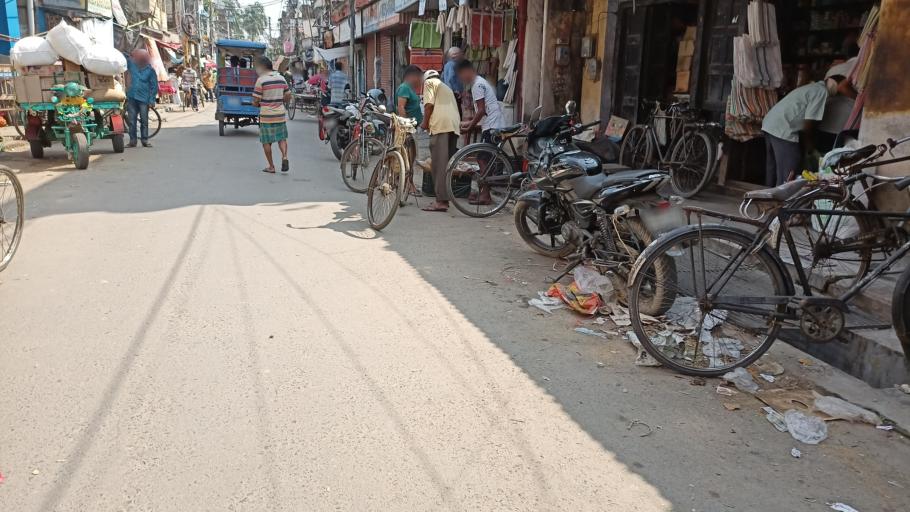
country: IN
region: West Bengal
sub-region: North 24 Parganas
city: Bangaon
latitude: 23.0455
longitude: 88.8307
